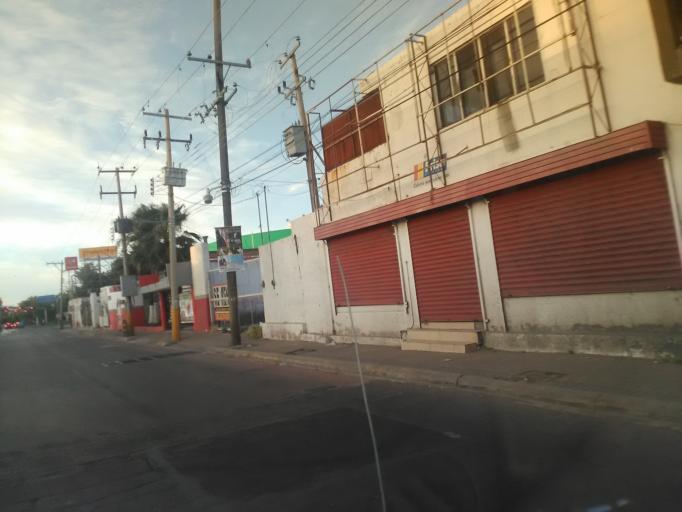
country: MX
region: Durango
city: Victoria de Durango
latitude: 24.0108
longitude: -104.6628
